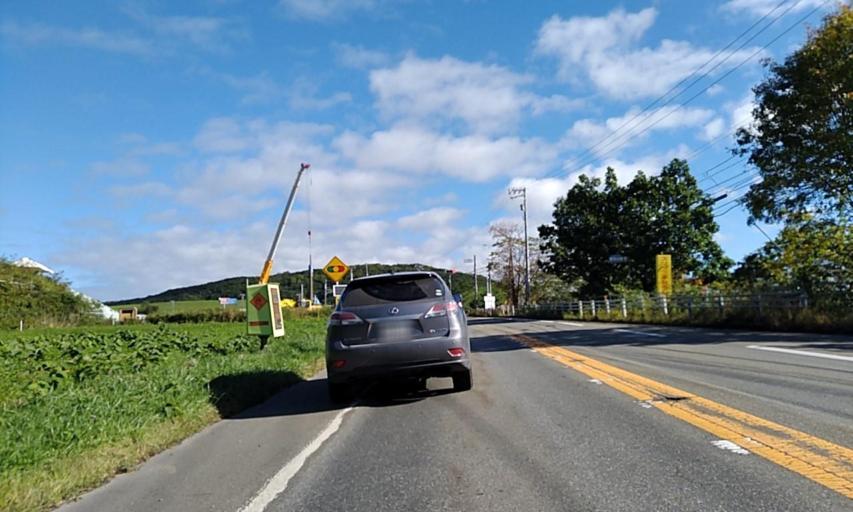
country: JP
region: Hokkaido
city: Shizunai-furukawacho
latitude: 42.3721
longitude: 142.3081
